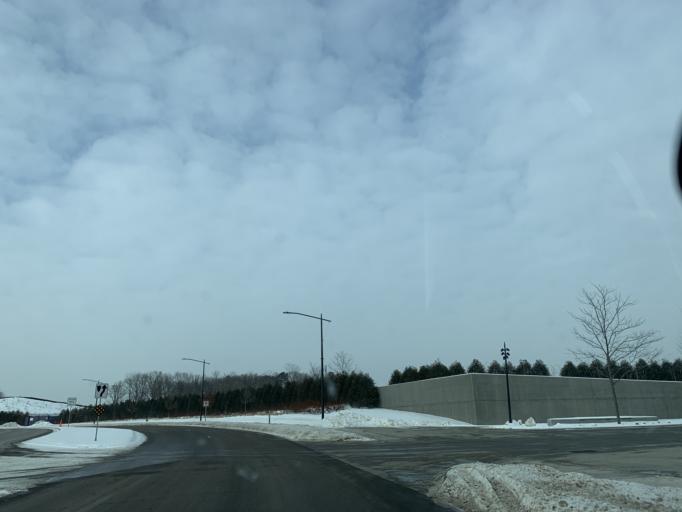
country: US
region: Minnesota
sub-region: Dakota County
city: Mendota Heights
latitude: 44.8585
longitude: -93.1187
